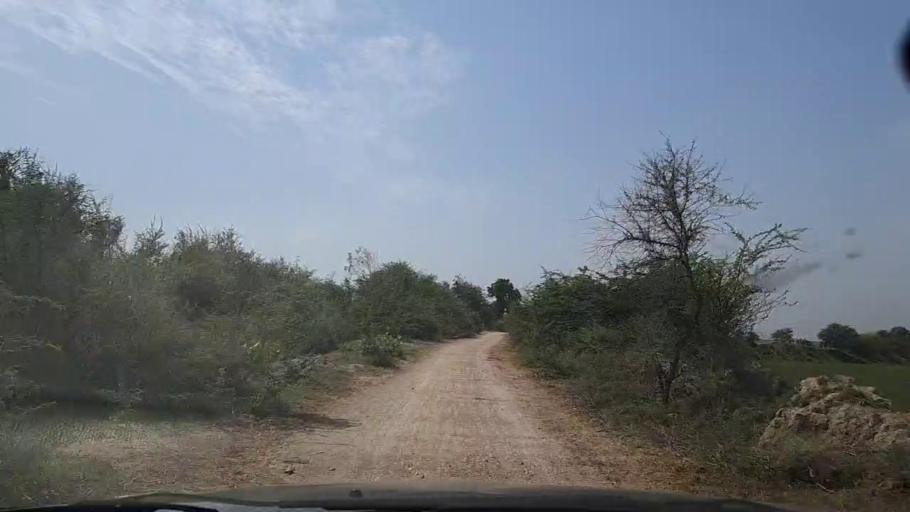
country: PK
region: Sindh
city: Mirpur Batoro
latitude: 24.6448
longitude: 68.1502
